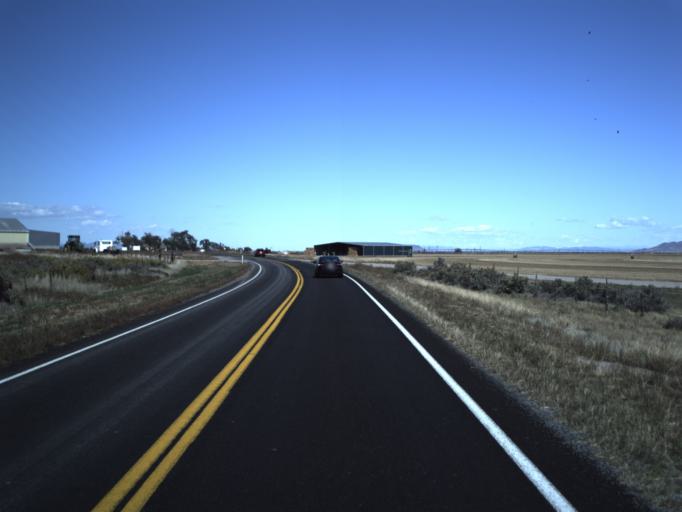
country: US
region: Utah
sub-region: Washington County
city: Enterprise
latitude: 37.6740
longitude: -113.6587
